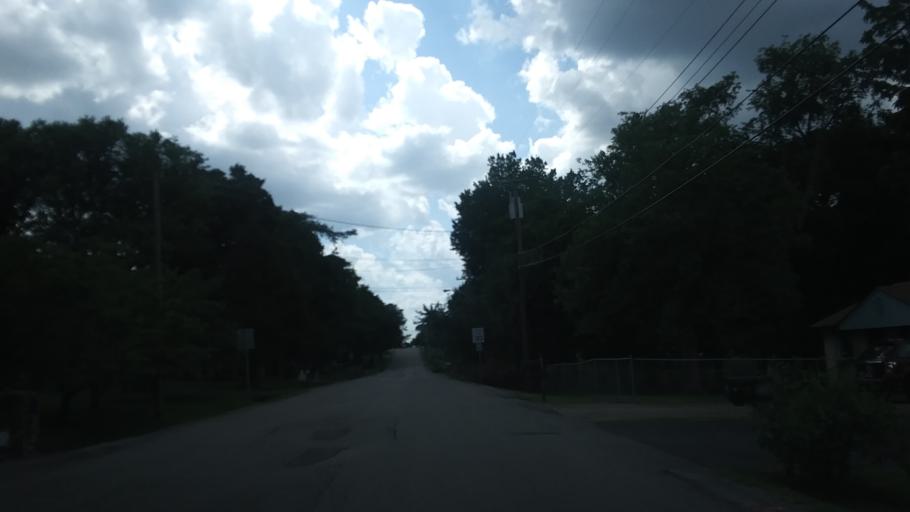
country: US
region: Tennessee
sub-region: Davidson County
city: Oak Hill
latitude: 36.0647
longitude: -86.7077
